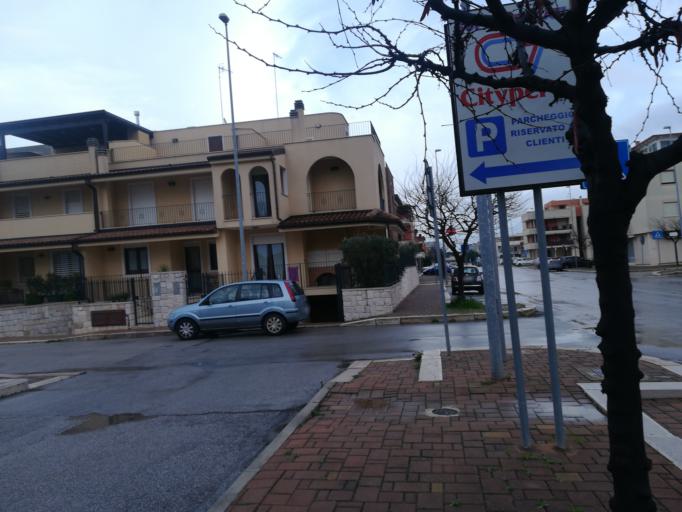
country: IT
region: Apulia
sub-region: Provincia di Bari
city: Polignano a Mare
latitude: 40.9939
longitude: 17.2115
